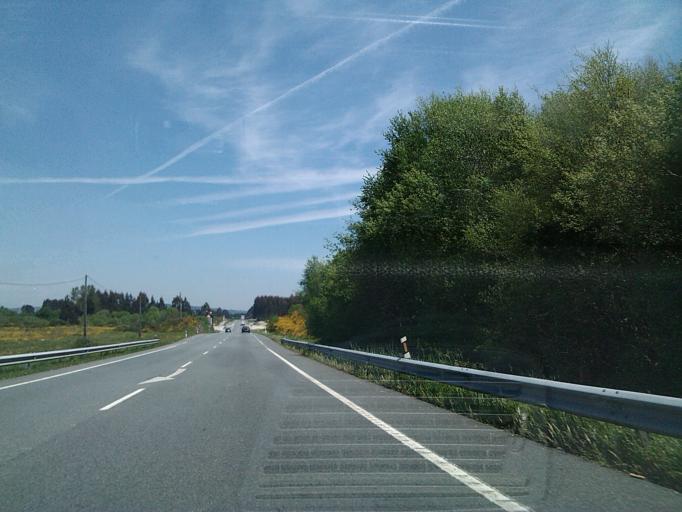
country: ES
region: Galicia
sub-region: Provincia da Coruna
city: Curtis
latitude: 43.1550
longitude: -8.0069
